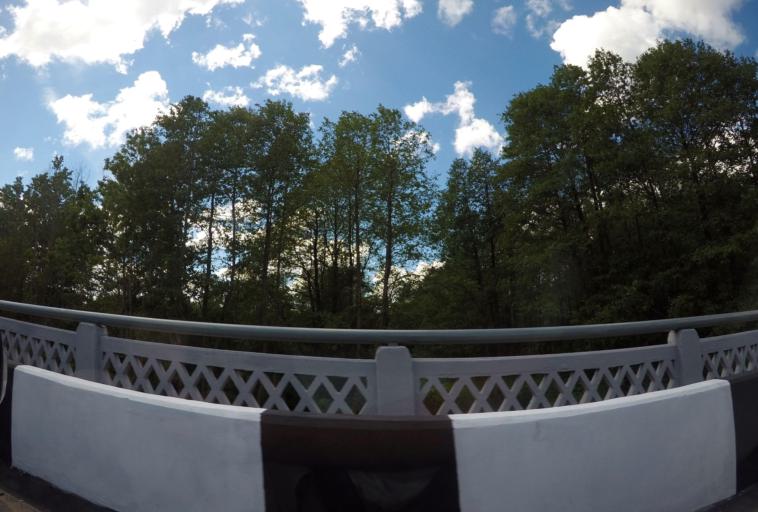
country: BY
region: Grodnenskaya
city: Hal'shany
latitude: 54.1929
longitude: 26.0895
